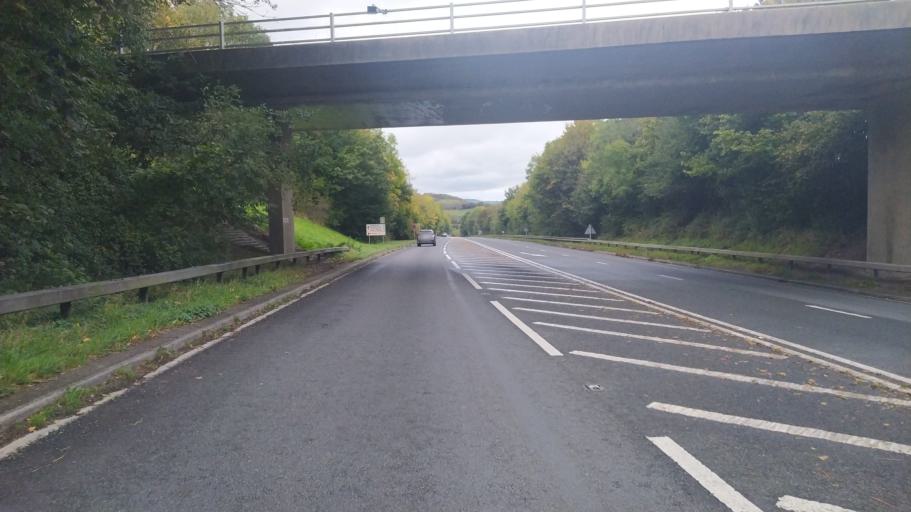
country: GB
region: England
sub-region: Dorset
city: Bridport
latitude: 50.7258
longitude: -2.7766
